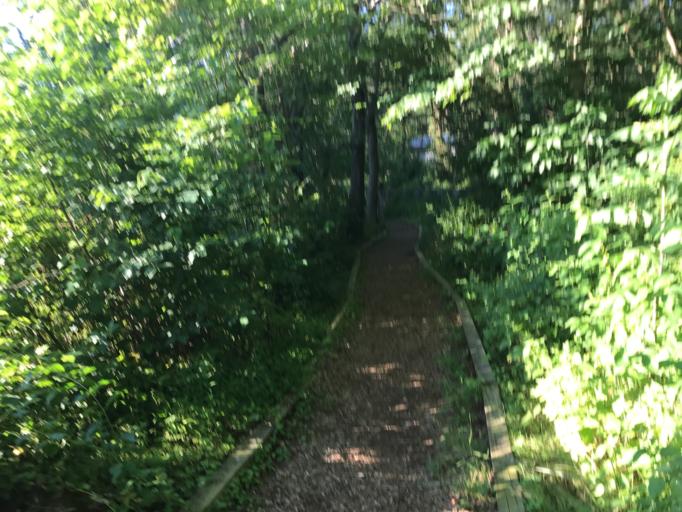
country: US
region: Maryland
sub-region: Harford County
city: Jarrettsville
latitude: 39.6767
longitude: -76.4542
